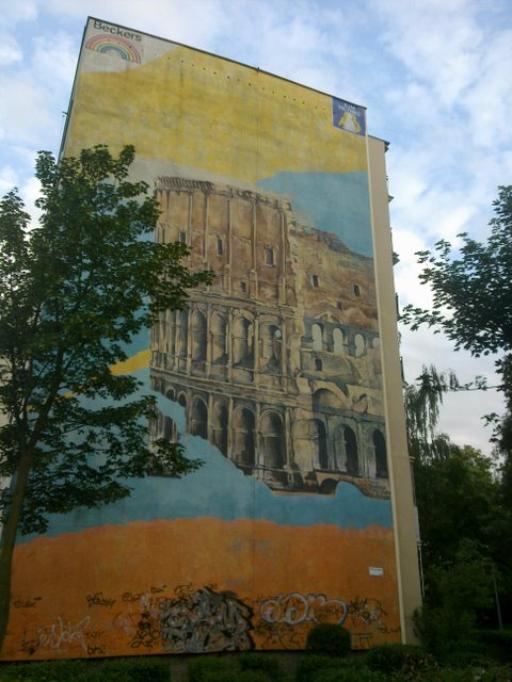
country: PL
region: Pomeranian Voivodeship
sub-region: Gdansk
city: Gdansk
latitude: 54.3924
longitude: 18.6034
